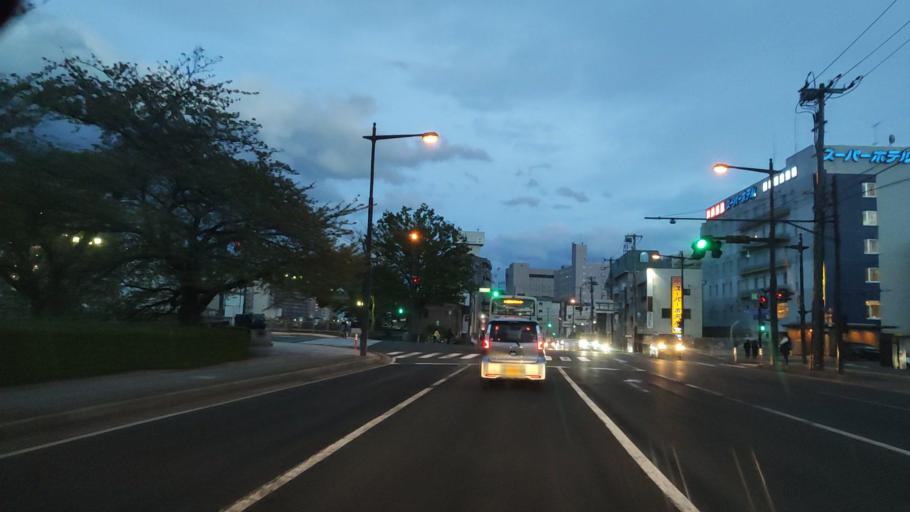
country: JP
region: Iwate
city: Morioka-shi
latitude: 39.7080
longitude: 141.1343
